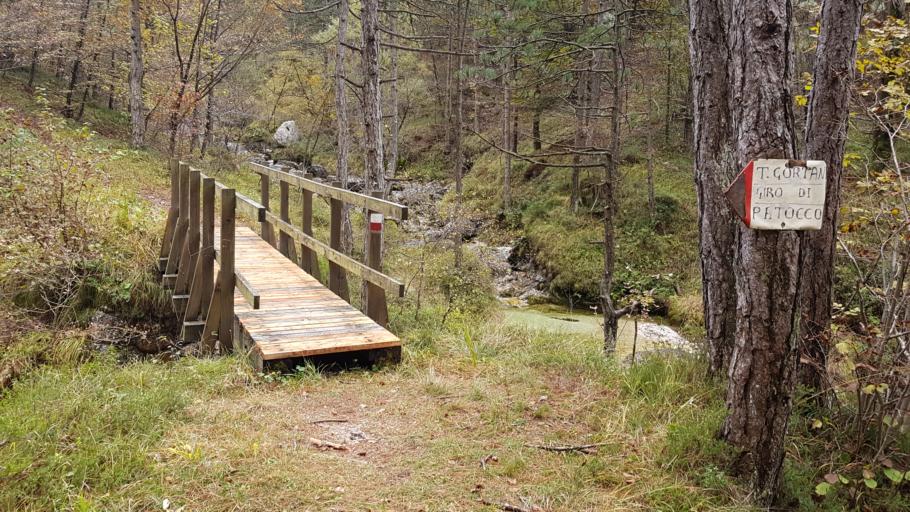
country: IT
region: Friuli Venezia Giulia
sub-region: Provincia di Udine
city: Chiusaforte
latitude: 46.4132
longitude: 13.3346
